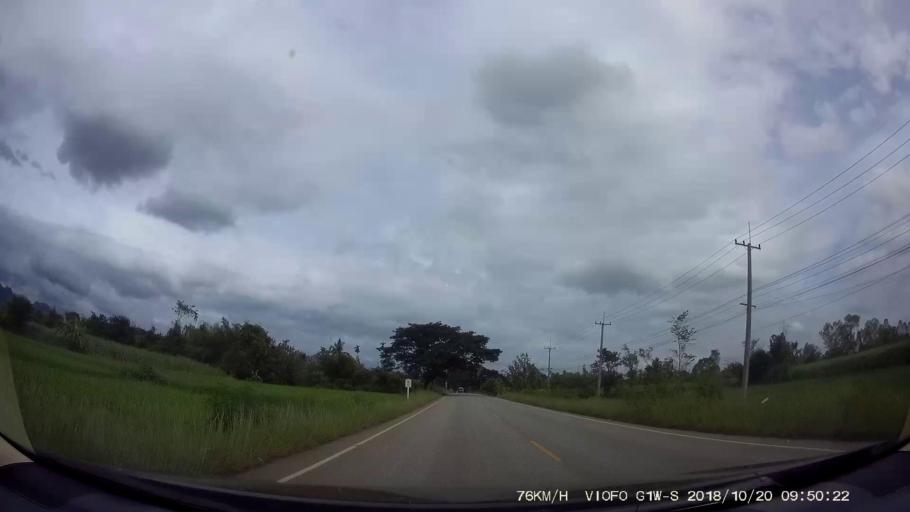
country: TH
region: Chaiyaphum
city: Khon San
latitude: 16.5303
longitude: 101.9024
